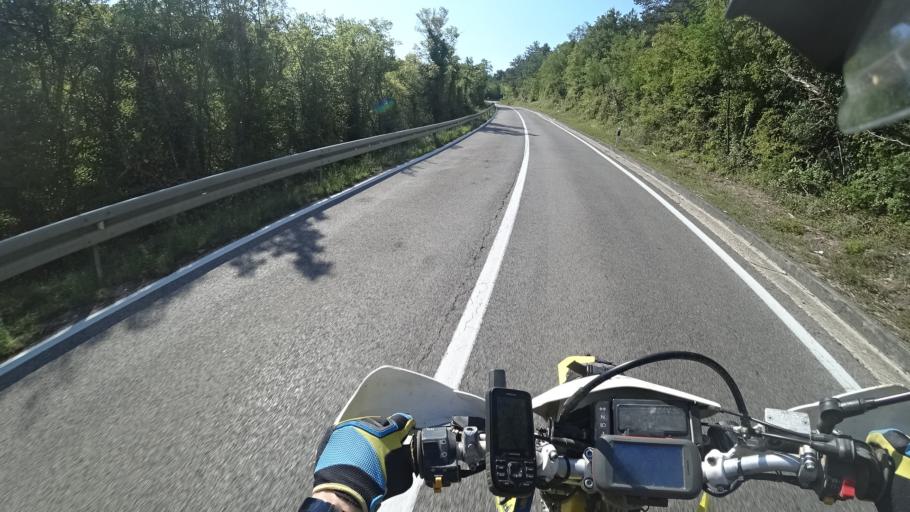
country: HR
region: Sibensko-Kniniska
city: Knin
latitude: 44.0184
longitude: 16.1951
